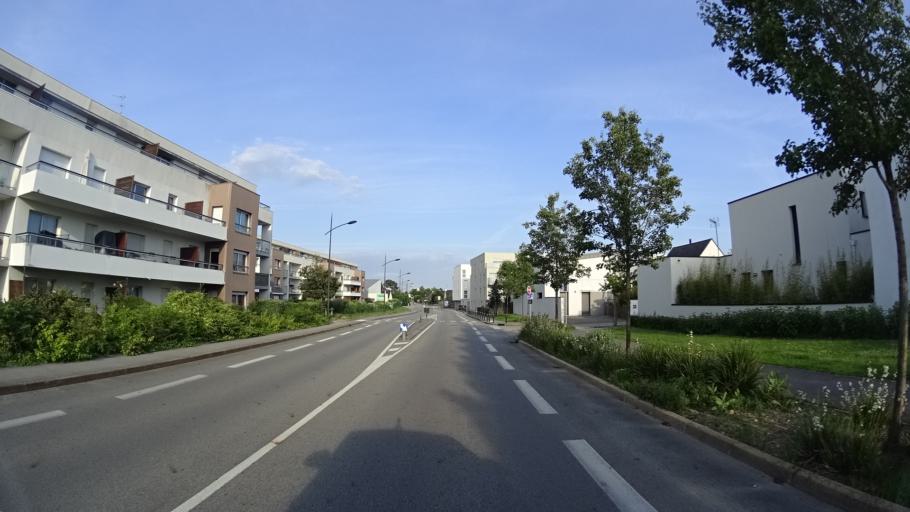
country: FR
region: Brittany
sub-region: Departement du Morbihan
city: Vannes
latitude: 47.6528
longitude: -2.7392
